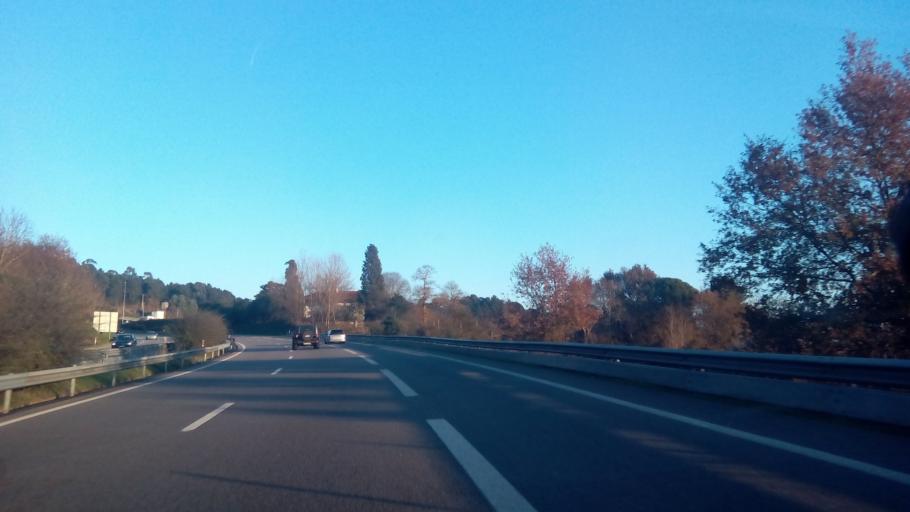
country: PT
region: Porto
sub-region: Marco de Canaveses
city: Marco de Canavezes
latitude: 41.2189
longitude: -8.1549
